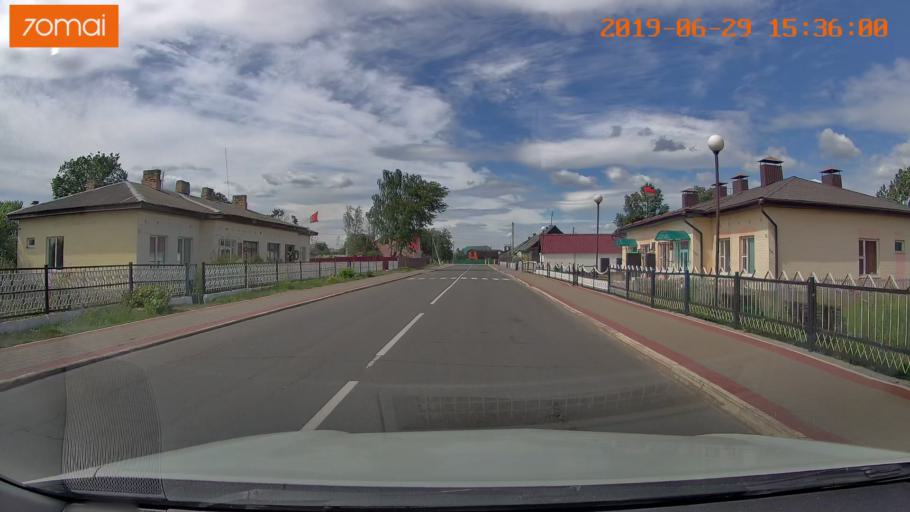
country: BY
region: Brest
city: Mikashevichy
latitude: 52.2181
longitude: 27.4704
